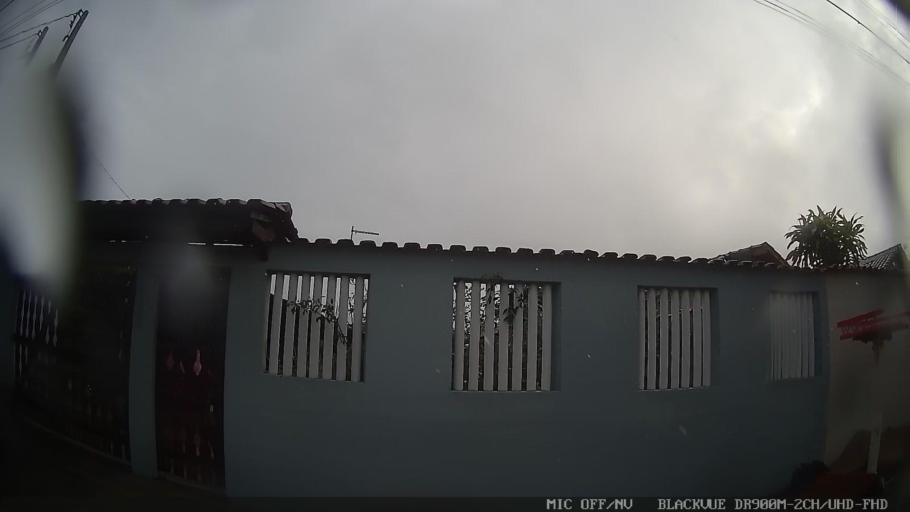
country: BR
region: Sao Paulo
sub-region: Itanhaem
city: Itanhaem
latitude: -24.2375
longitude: -46.9016
